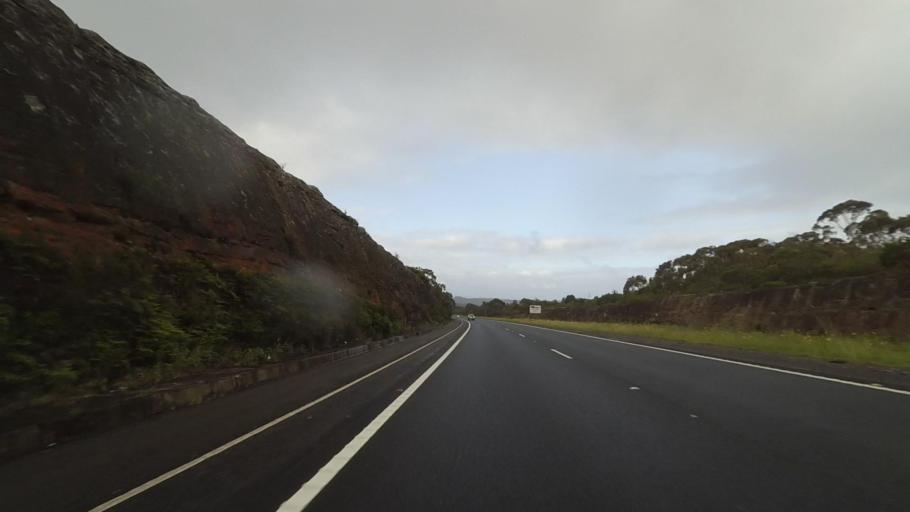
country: AU
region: New South Wales
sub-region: Wollongong
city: Helensburgh
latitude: -34.2380
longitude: 150.9459
